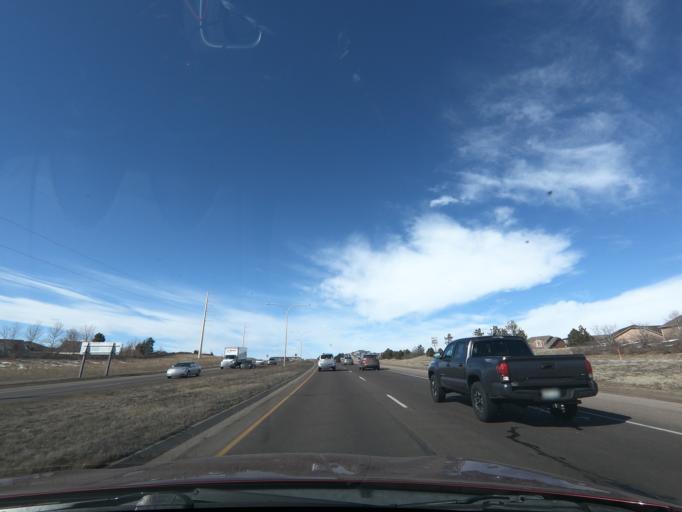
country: US
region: Colorado
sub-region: El Paso County
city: Black Forest
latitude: 38.9520
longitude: -104.7222
